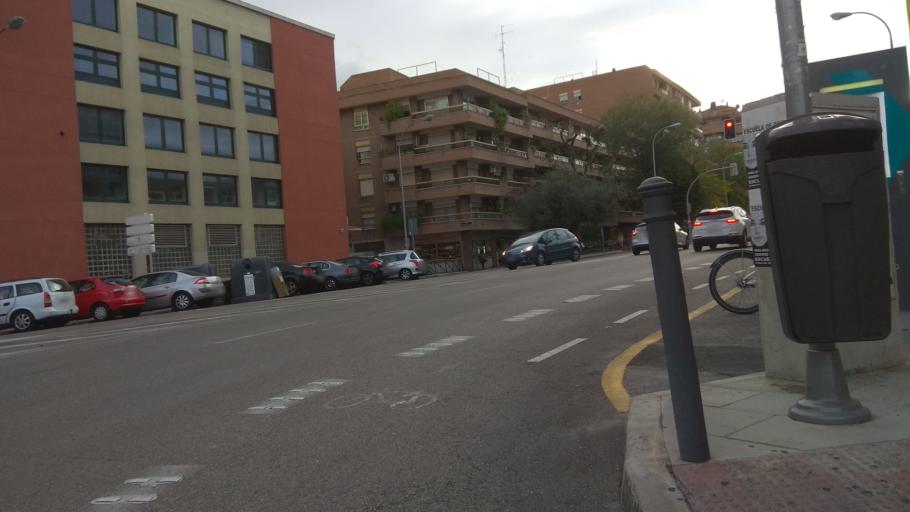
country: ES
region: Madrid
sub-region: Provincia de Madrid
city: Salamanca
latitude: 40.4327
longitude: -3.6650
